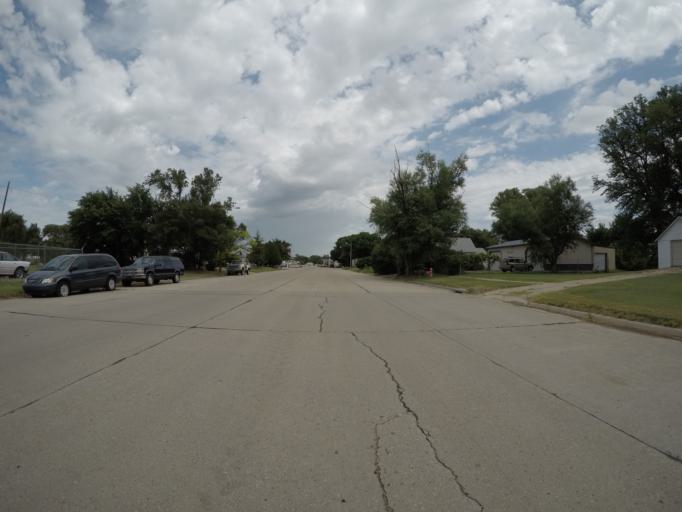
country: US
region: Kansas
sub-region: Rawlins County
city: Atwood
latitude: 39.8065
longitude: -101.0464
